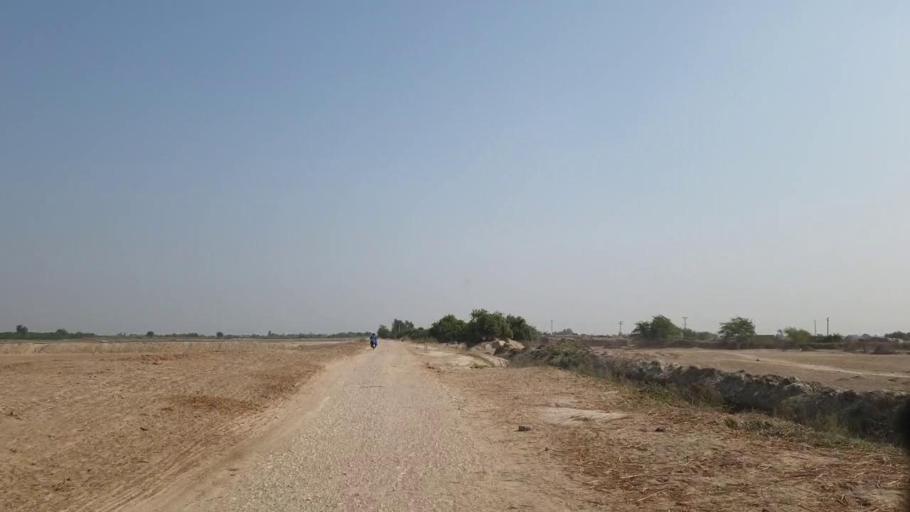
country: PK
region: Sindh
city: Bulri
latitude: 24.9356
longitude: 68.3623
